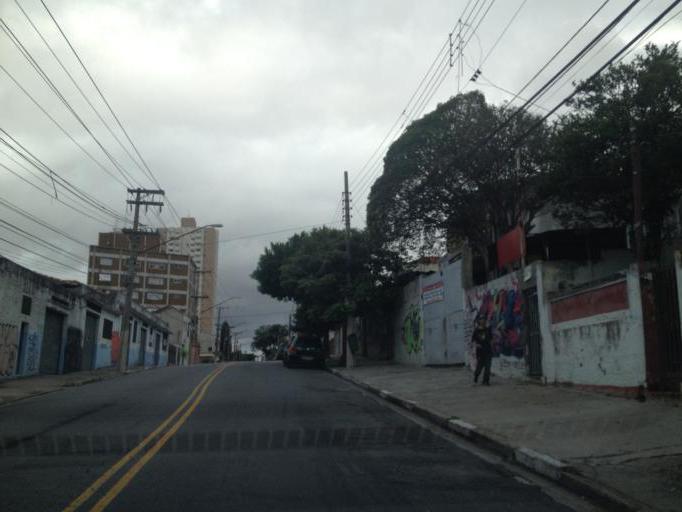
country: BR
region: Sao Paulo
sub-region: Sao Paulo
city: Sao Paulo
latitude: -23.5584
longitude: -46.5843
